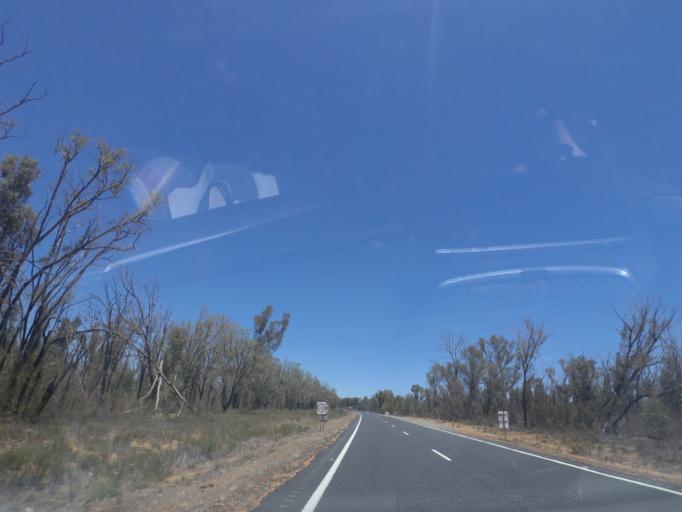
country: AU
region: New South Wales
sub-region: Warrumbungle Shire
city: Coonabarabran
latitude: -30.9416
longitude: 149.4236
